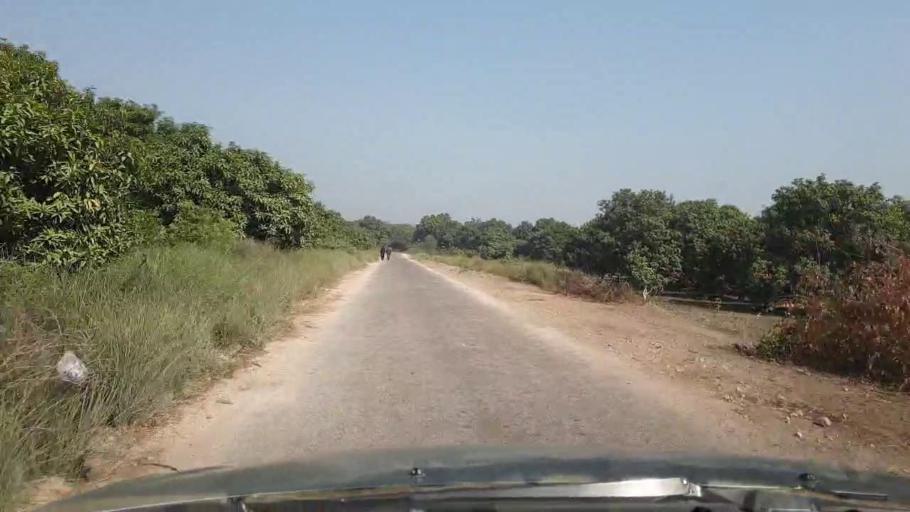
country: PK
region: Sindh
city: Tando Jam
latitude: 25.3258
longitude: 68.5406
